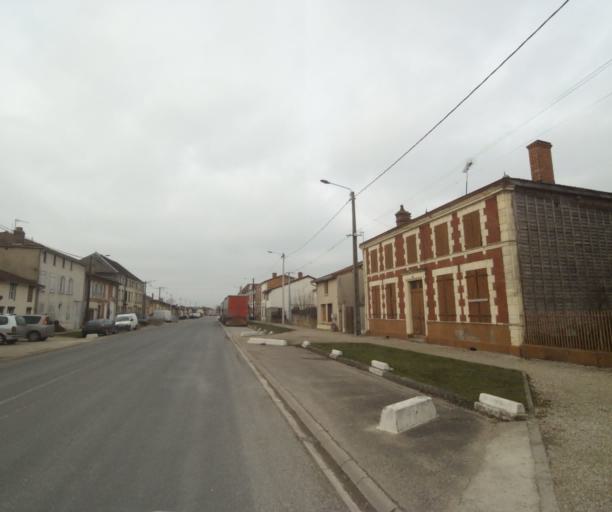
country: FR
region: Champagne-Ardenne
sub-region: Departement de la Haute-Marne
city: Villiers-en-Lieu
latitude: 48.6553
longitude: 4.8233
